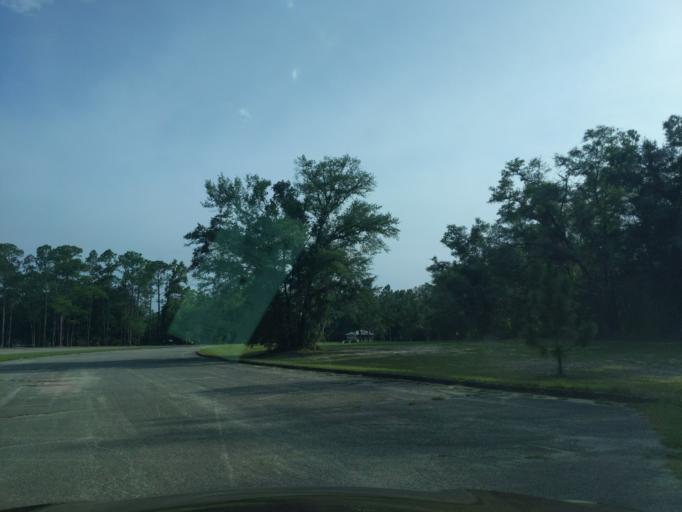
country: US
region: Florida
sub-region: Gadsden County
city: Midway
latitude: 30.4054
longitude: -84.4075
